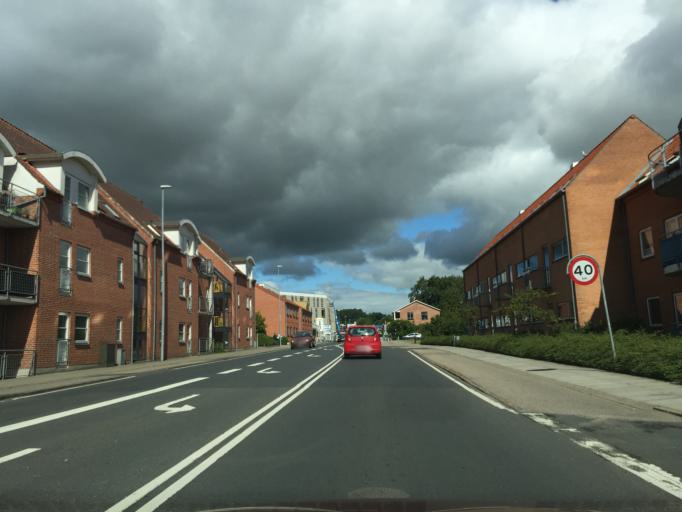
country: DK
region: Central Jutland
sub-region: Silkeborg Kommune
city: Silkeborg
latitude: 56.1821
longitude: 9.5477
